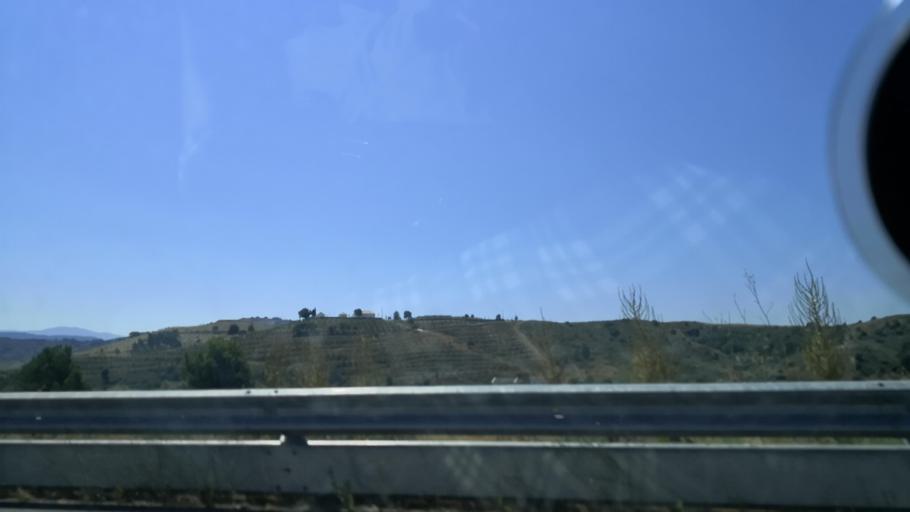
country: PT
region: Braganca
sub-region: Mirandela
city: Mirandela
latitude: 41.5160
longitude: -7.1547
